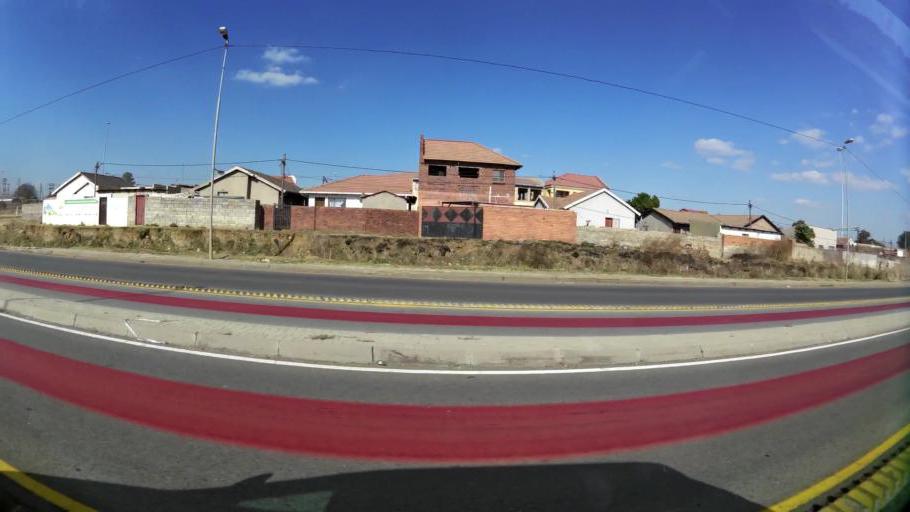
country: ZA
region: Gauteng
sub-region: City of Johannesburg Metropolitan Municipality
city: Soweto
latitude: -26.2557
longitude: 27.8931
